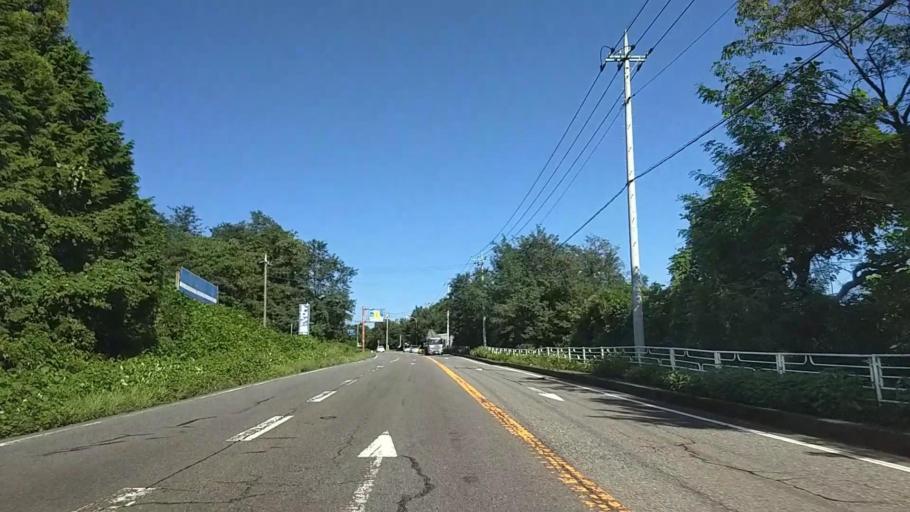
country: JP
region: Gunma
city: Annaka
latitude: 36.3114
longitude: 138.8134
